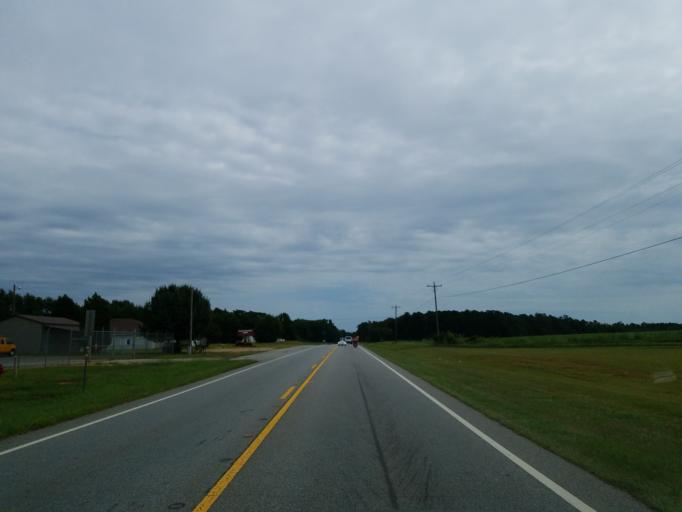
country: US
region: Georgia
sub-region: Lamar County
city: Barnesville
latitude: 33.0137
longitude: -84.1287
